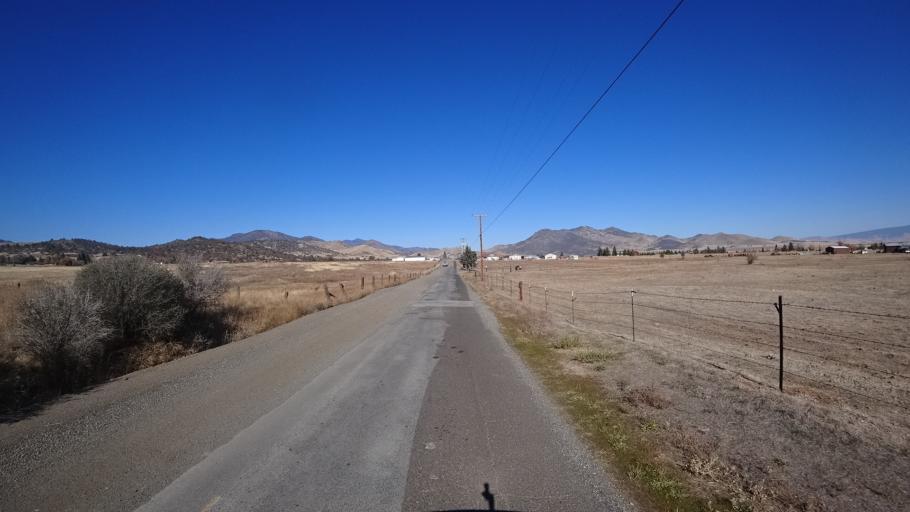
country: US
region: California
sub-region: Siskiyou County
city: Yreka
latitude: 41.7384
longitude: -122.5932
